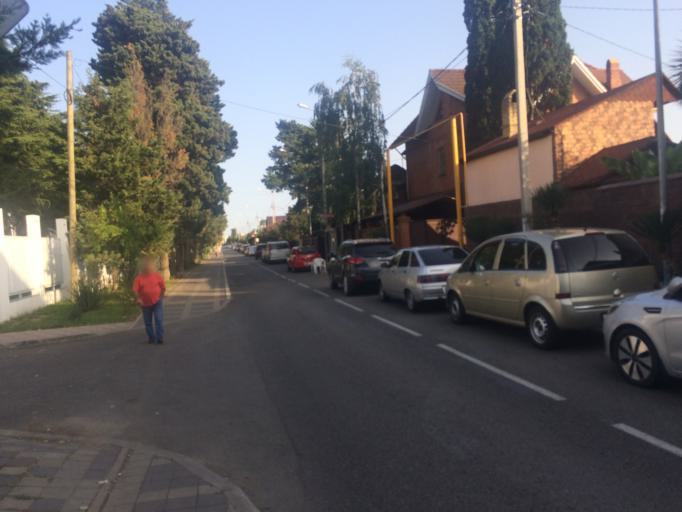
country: RU
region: Krasnodarskiy
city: Adler
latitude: 43.3894
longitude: 39.9871
